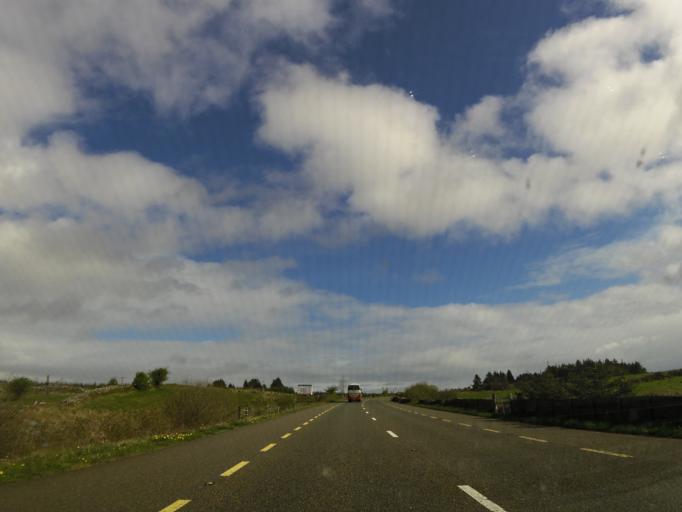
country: IE
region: Connaught
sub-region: Maigh Eo
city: Ballyhaunis
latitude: 53.8983
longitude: -8.7992
